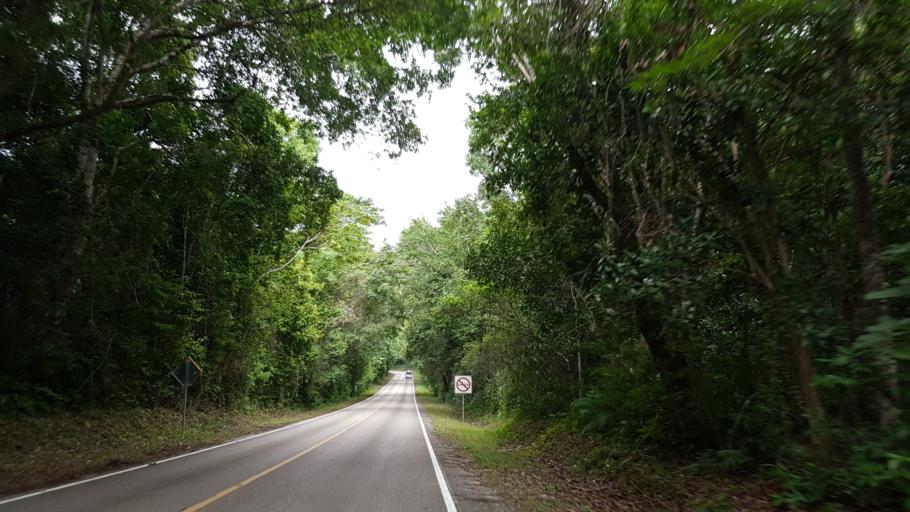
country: GT
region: Peten
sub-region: Municipio de San Jose
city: San Jose
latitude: 17.2095
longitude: -89.6192
